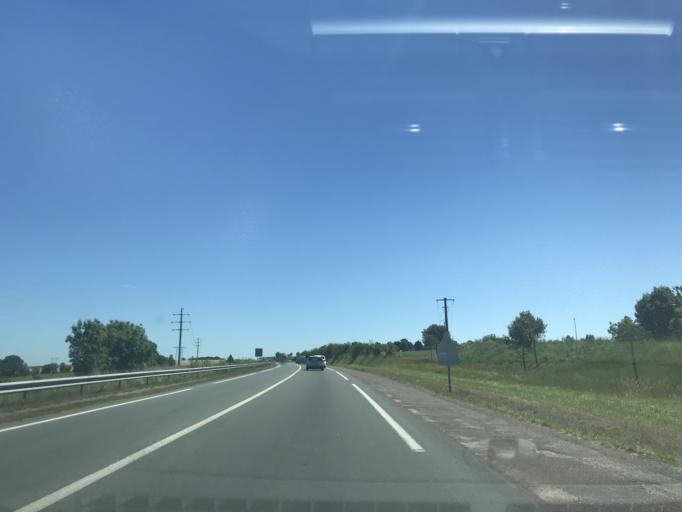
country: FR
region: Poitou-Charentes
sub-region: Departement de la Charente-Maritime
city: Saint-Georges-de-Didonne
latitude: 45.6156
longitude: -0.9872
